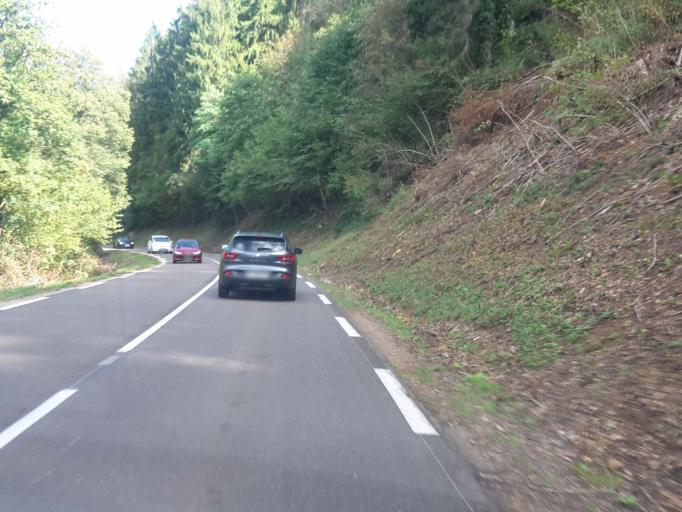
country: FR
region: Franche-Comte
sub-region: Departement du Doubs
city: Baume-les-Dames
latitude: 47.3404
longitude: 6.3769
